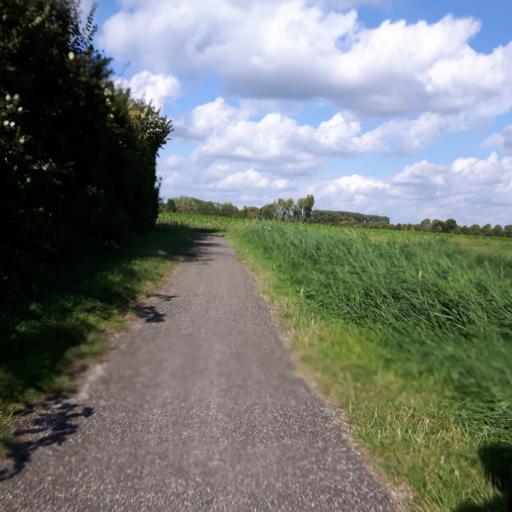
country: NL
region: Zeeland
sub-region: Gemeente Goes
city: Goes
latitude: 51.4882
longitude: 3.8307
